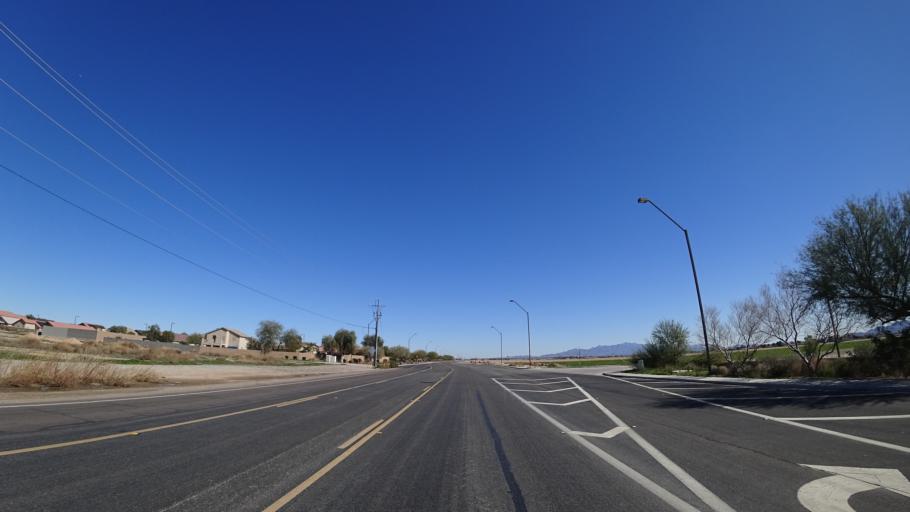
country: US
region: Arizona
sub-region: Maricopa County
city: Buckeye
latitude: 33.3920
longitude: -112.5895
